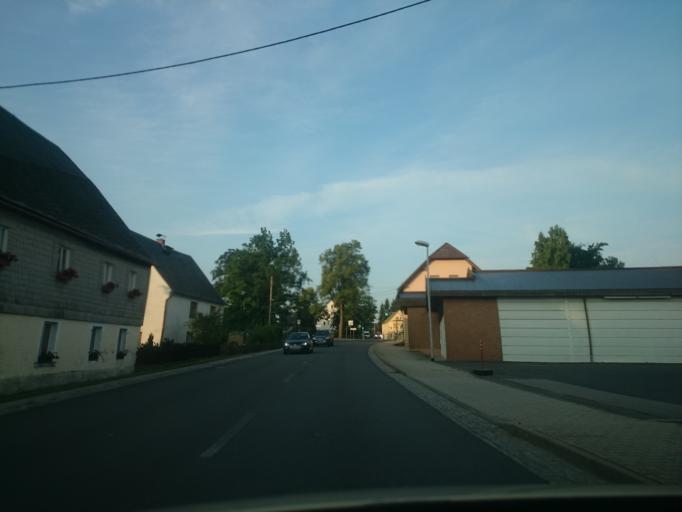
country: DE
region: Saxony
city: Grosshartmannsdorf
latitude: 50.7992
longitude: 13.3203
